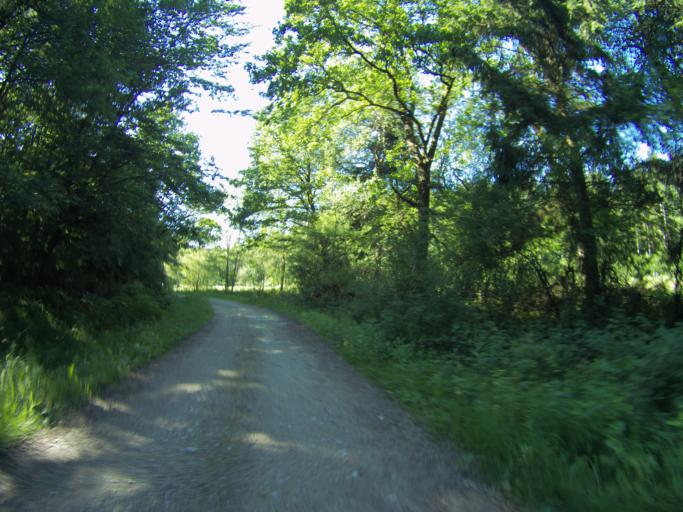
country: DE
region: Bavaria
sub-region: Upper Bavaria
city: Kirchdorf
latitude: 48.4106
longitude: 11.6838
